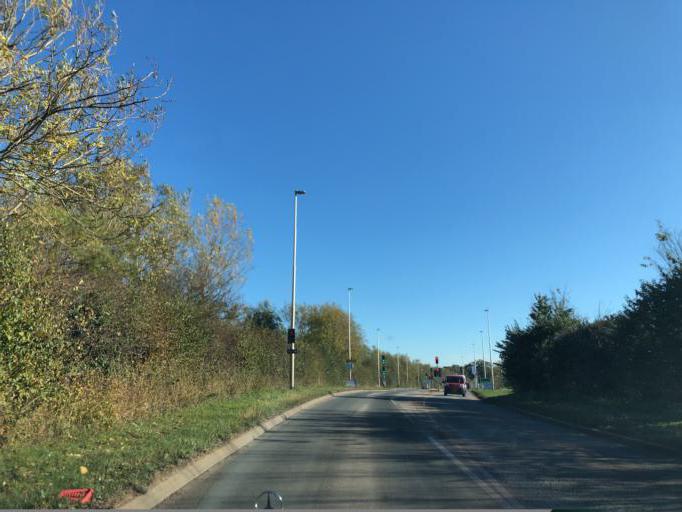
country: GB
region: England
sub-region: Warwickshire
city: Royal Leamington Spa
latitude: 52.2631
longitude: -1.5433
